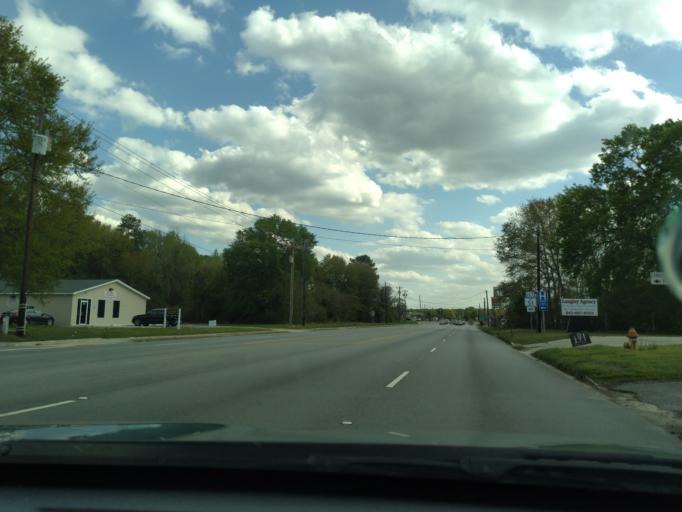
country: US
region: South Carolina
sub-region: Florence County
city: Florence
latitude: 34.1667
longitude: -79.7603
